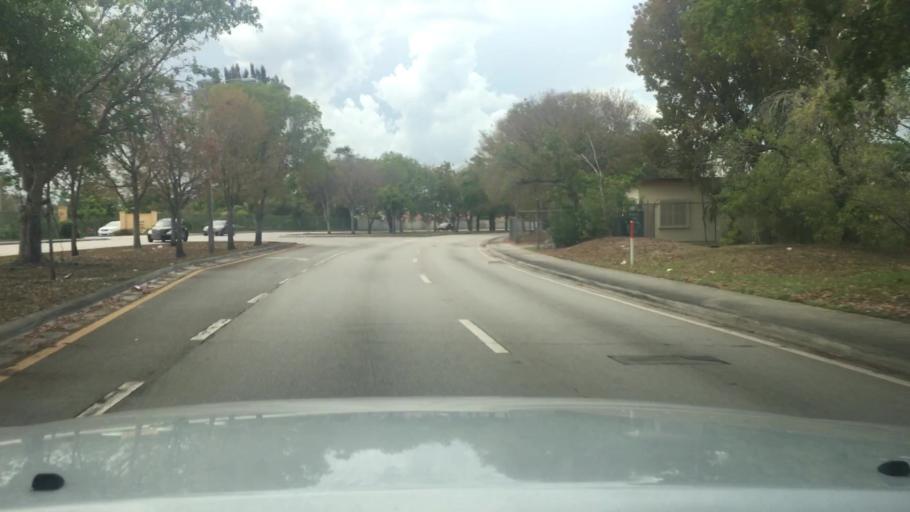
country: US
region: Florida
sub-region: Miami-Dade County
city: Tamiami
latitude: 25.7564
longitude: -80.3917
